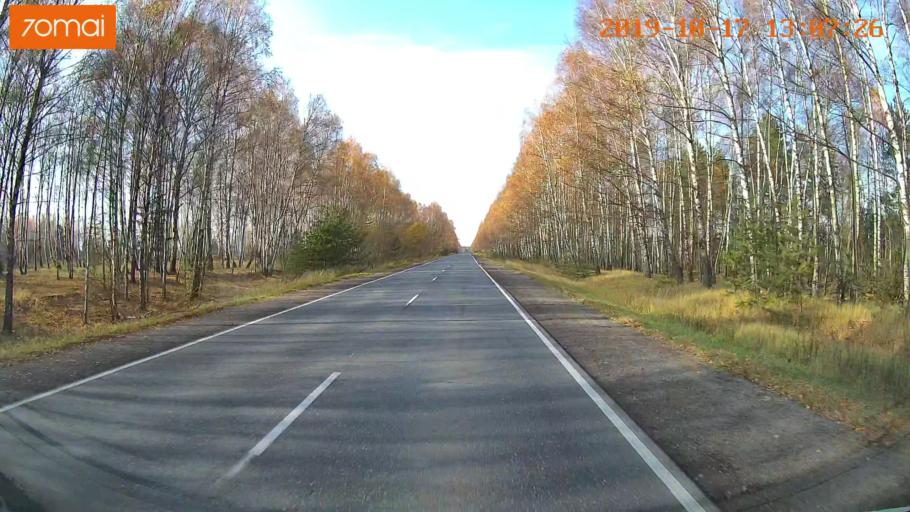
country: RU
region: Rjazan
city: Syntul
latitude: 54.9821
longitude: 41.2907
